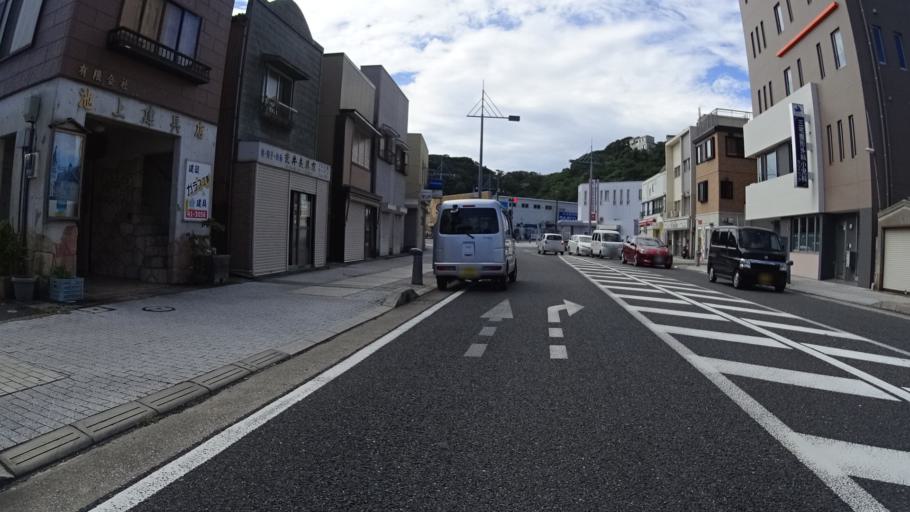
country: JP
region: Kanagawa
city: Yokosuka
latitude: 35.2472
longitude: 139.7149
